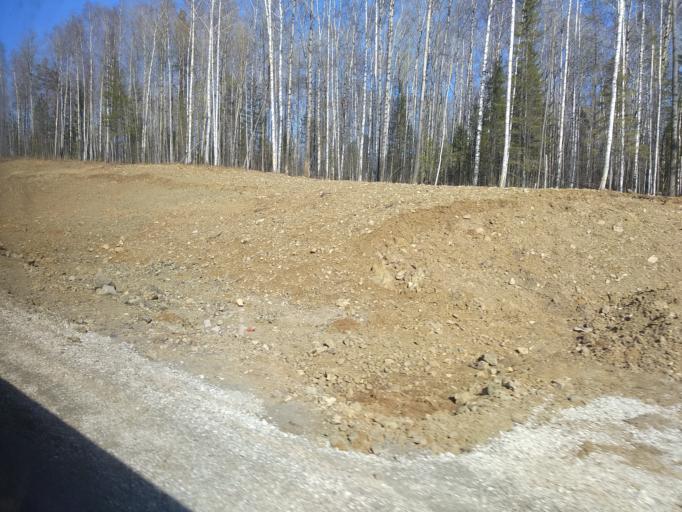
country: RU
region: Sverdlovsk
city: Krasnotur'insk
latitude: 59.6695
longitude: 60.1817
